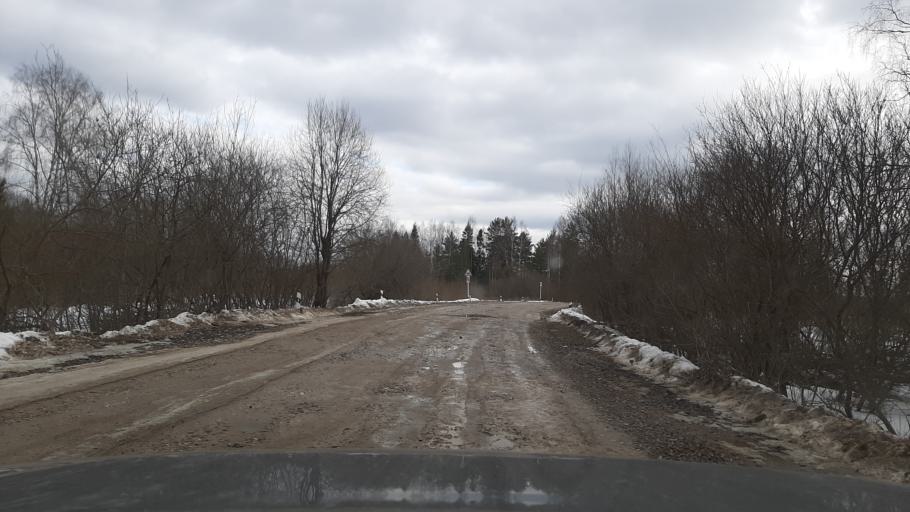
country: RU
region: Ivanovo
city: Teykovo
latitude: 56.8846
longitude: 40.6208
